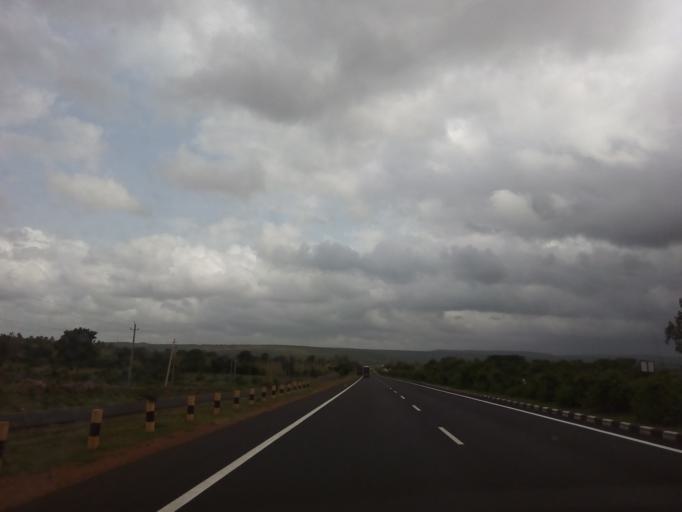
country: IN
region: Karnataka
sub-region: Belgaum
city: Hukeri
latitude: 16.0878
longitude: 74.5185
